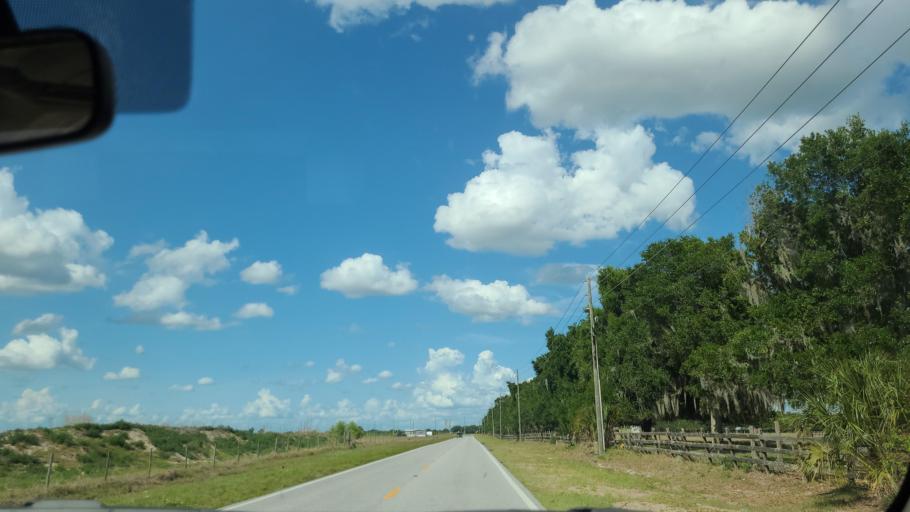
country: US
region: Florida
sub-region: Polk County
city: Lake Wales
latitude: 27.9207
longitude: -81.5437
